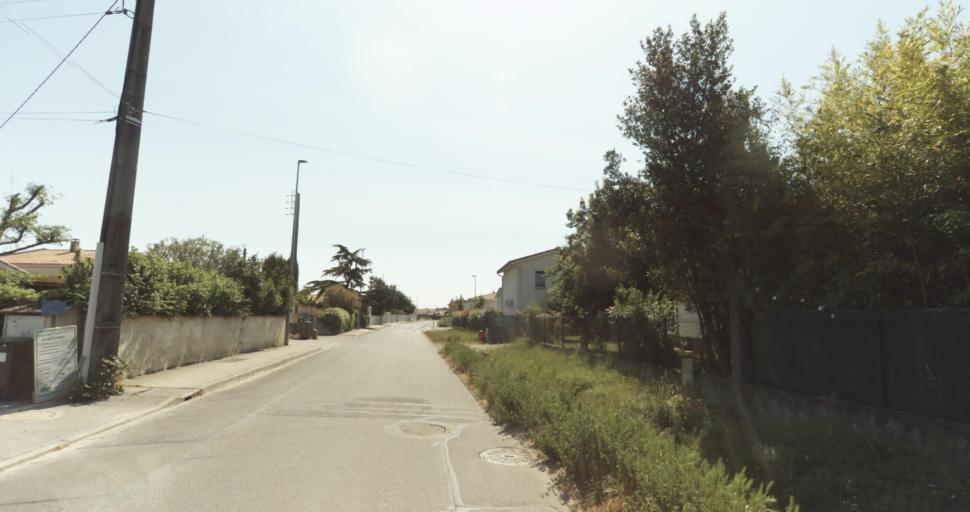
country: FR
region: Midi-Pyrenees
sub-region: Departement de la Haute-Garonne
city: La Salvetat-Saint-Gilles
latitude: 43.5790
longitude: 1.2785
